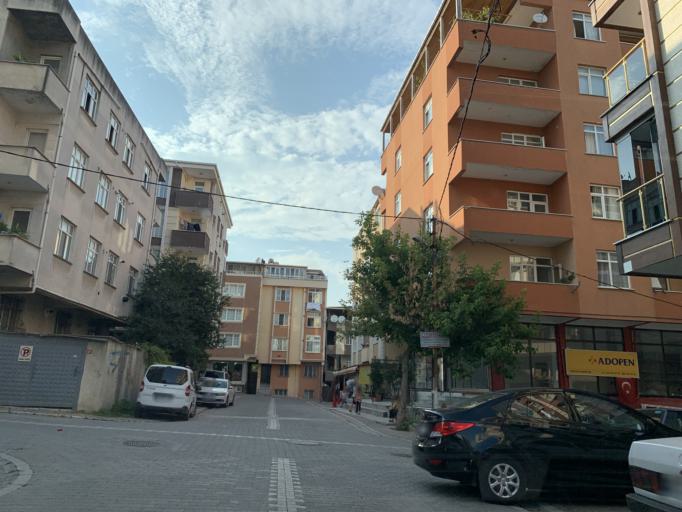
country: TR
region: Istanbul
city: Esenyurt
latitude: 41.0409
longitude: 28.6817
